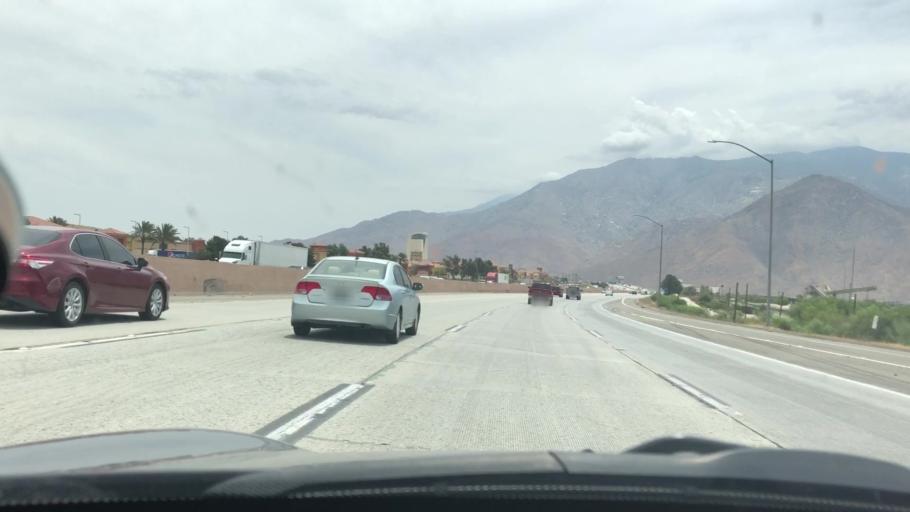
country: US
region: California
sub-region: Riverside County
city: Cabazon
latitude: 33.9300
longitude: -116.8194
